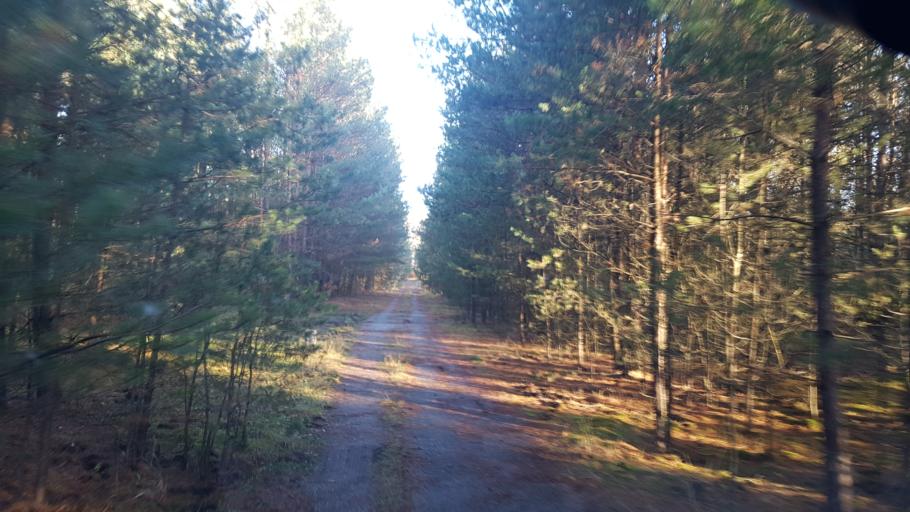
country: DE
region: Brandenburg
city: Crinitz
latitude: 51.7259
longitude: 13.7459
